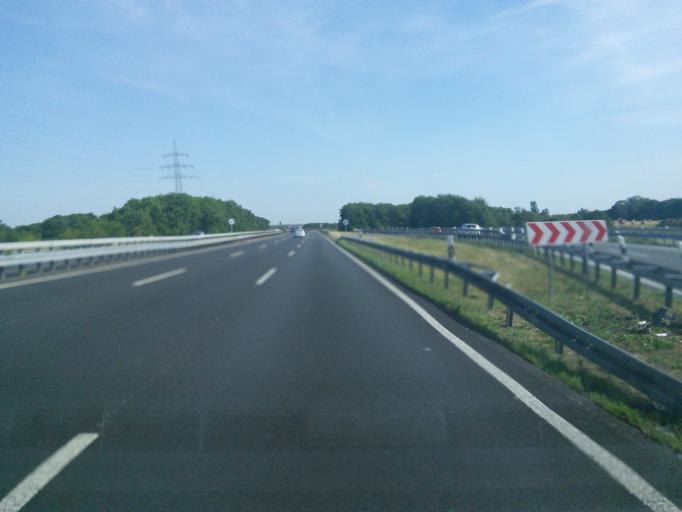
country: DE
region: North Rhine-Westphalia
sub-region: Regierungsbezirk Dusseldorf
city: Dusseldorf
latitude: 51.1552
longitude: 6.7514
